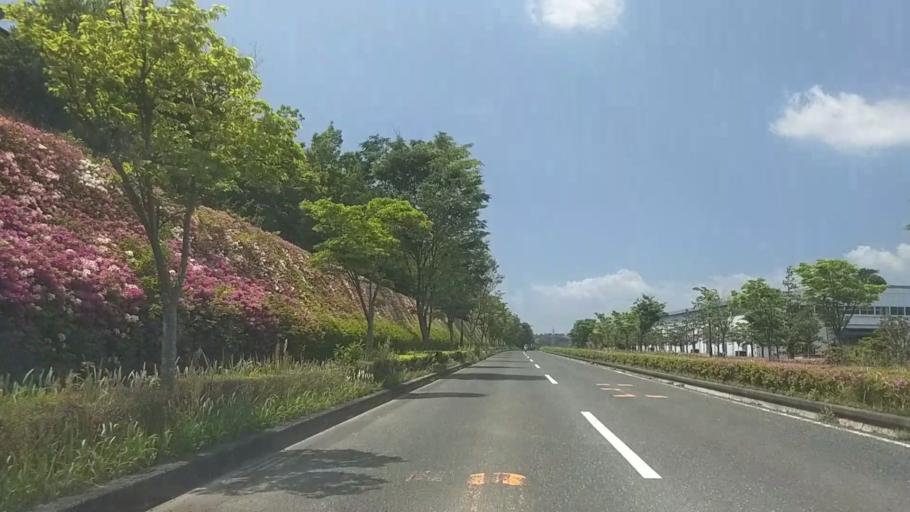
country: JP
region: Shizuoka
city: Hamamatsu
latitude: 34.7705
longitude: 137.6784
